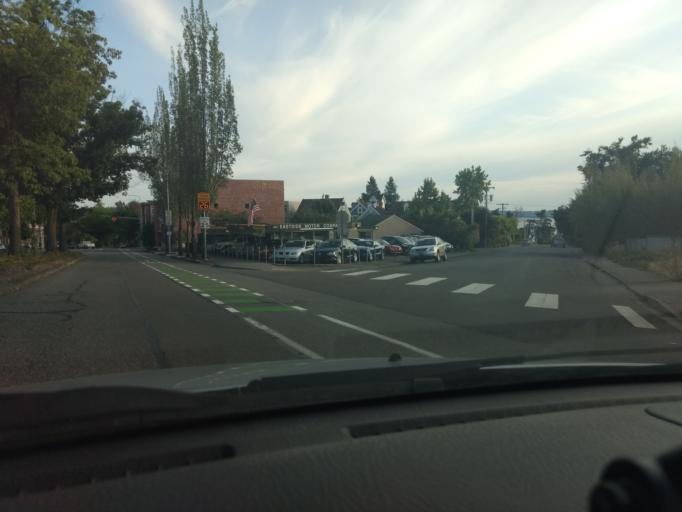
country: US
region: Washington
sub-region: King County
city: Kirkland
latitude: 47.6816
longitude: -122.2097
